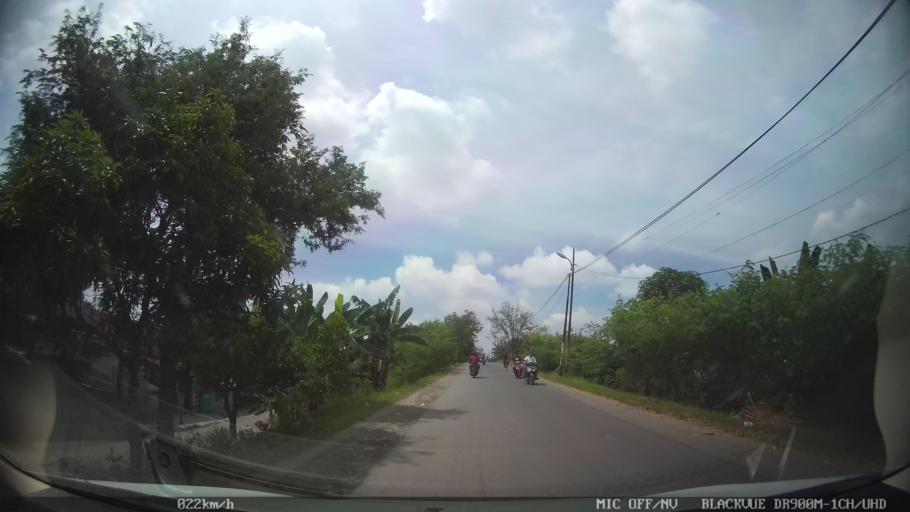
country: ID
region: North Sumatra
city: Medan
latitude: 3.6472
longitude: 98.6877
